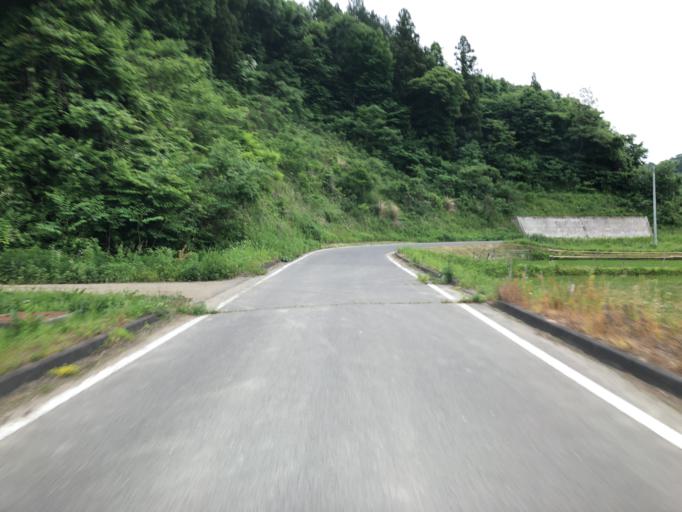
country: JP
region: Fukushima
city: Funehikimachi-funehiki
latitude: 37.4527
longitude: 140.5297
